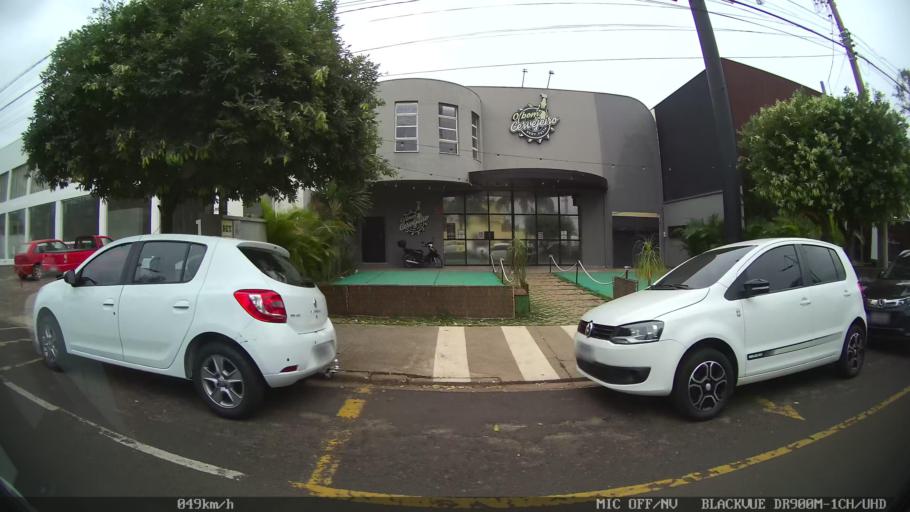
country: BR
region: Sao Paulo
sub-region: Sao Jose Do Rio Preto
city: Sao Jose do Rio Preto
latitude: -20.8389
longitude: -49.4013
